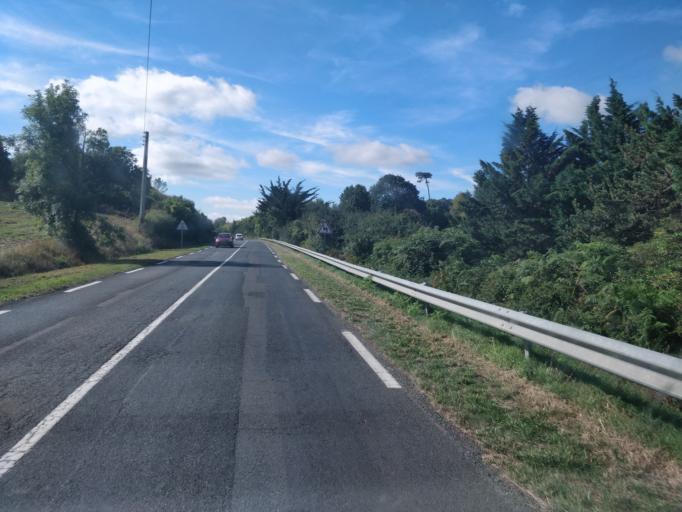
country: FR
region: Brittany
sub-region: Departement des Cotes-d'Armor
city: Erquy
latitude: 48.6183
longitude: -2.4731
